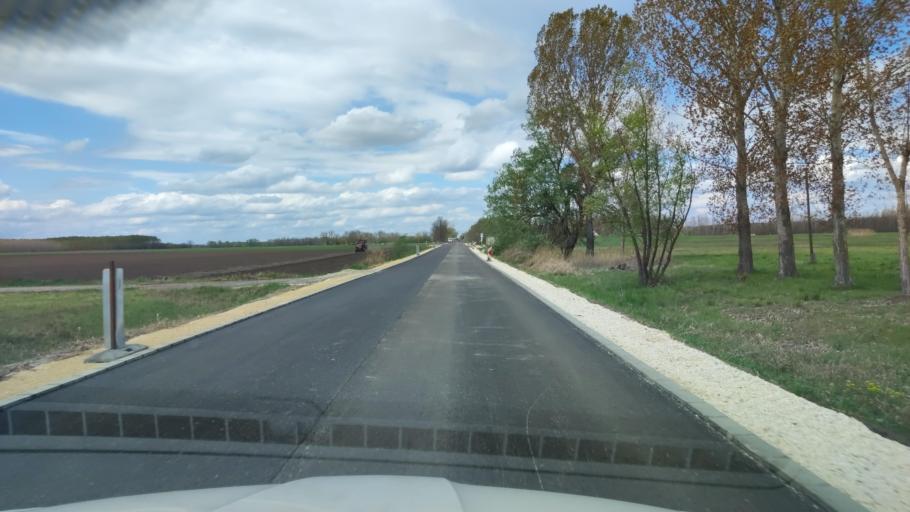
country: HU
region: Pest
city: Kocser
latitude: 46.9881
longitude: 19.9730
